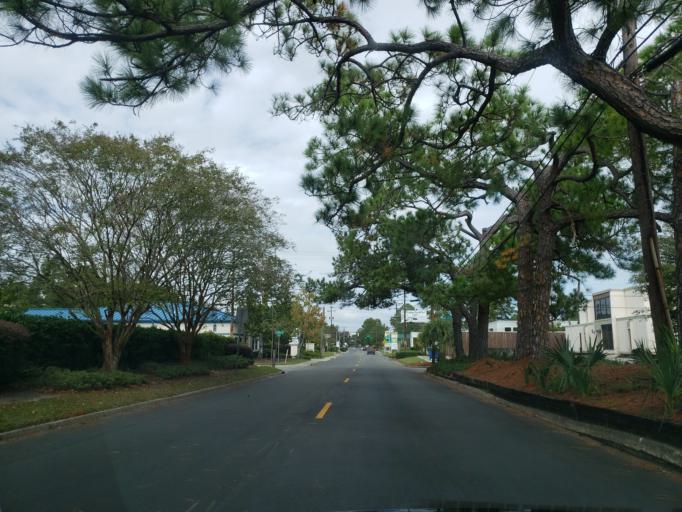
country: US
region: Georgia
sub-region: Chatham County
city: Thunderbolt
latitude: 32.0290
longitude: -81.0965
